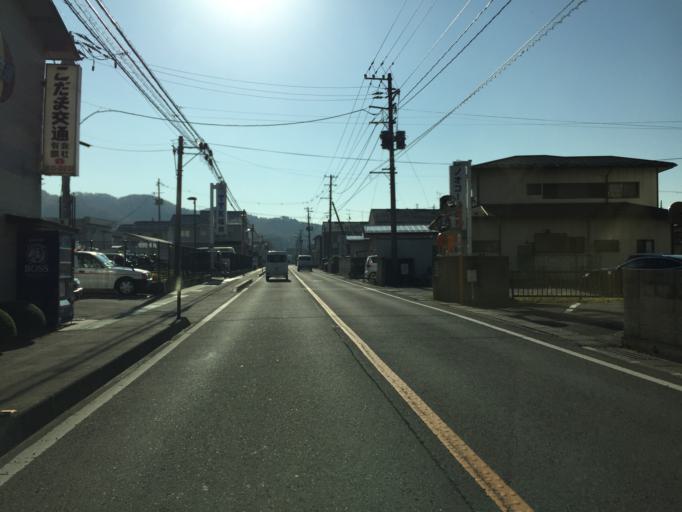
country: JP
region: Fukushima
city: Fukushima-shi
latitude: 37.7354
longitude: 140.4732
